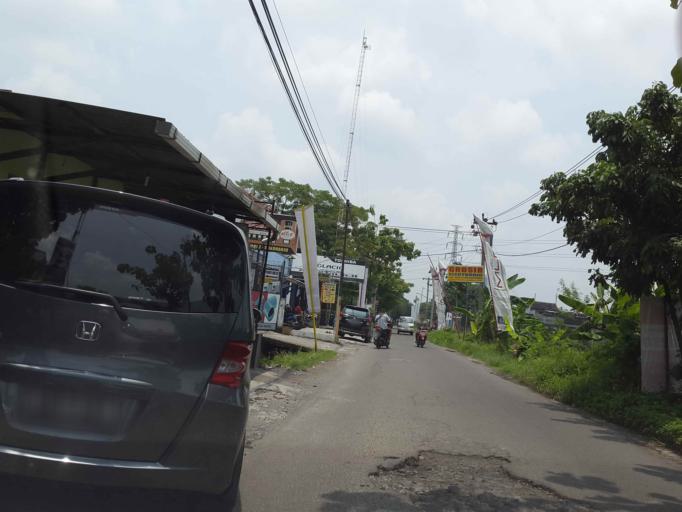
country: ID
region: Central Java
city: Colomadu
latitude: -7.5527
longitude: 110.7732
